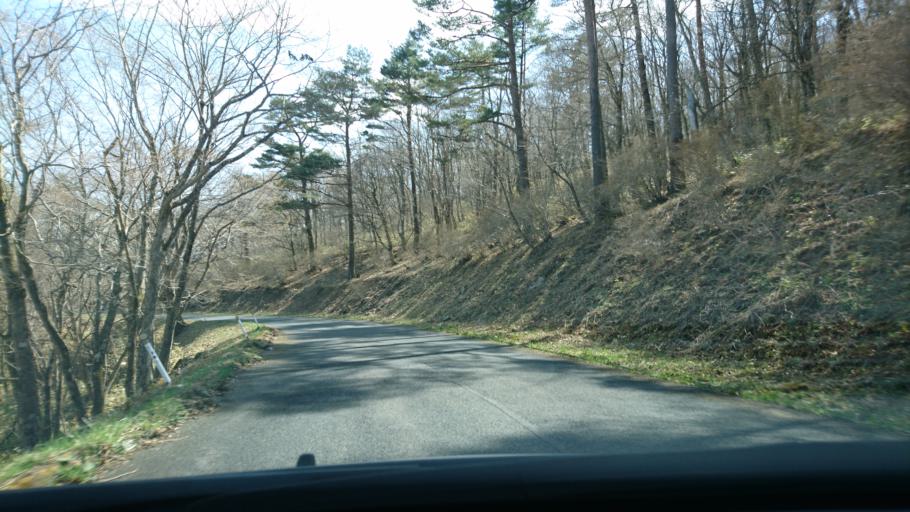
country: JP
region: Iwate
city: Ofunato
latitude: 38.9710
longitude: 141.4547
